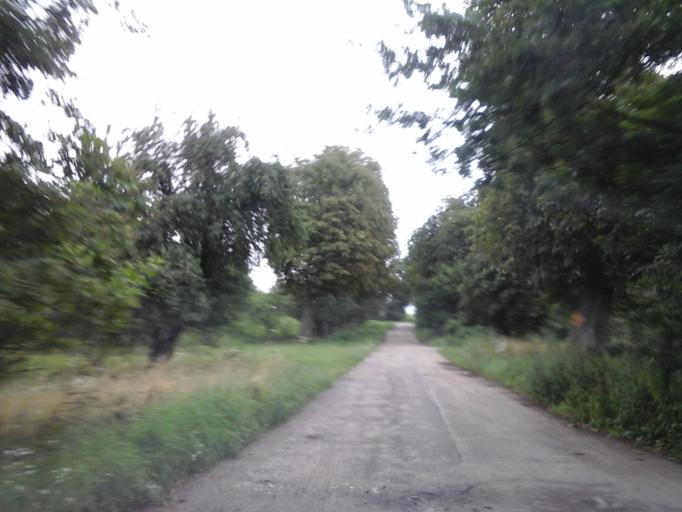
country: PL
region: West Pomeranian Voivodeship
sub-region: Powiat choszczenski
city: Krzecin
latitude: 52.9730
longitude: 15.4255
